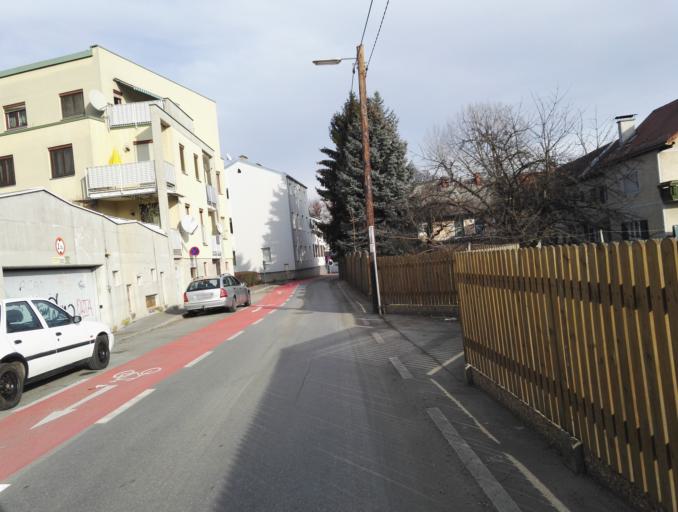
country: AT
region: Styria
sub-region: Graz Stadt
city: Graz
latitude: 47.0620
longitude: 15.4265
